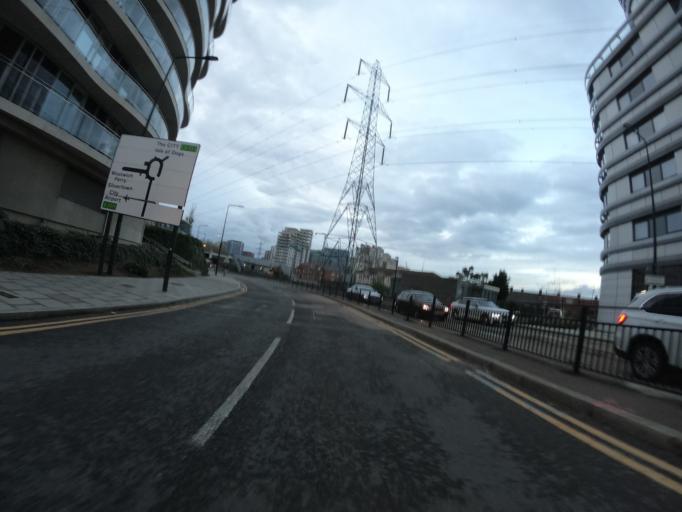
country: GB
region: England
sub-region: Greater London
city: Poplar
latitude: 51.5085
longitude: 0.0159
